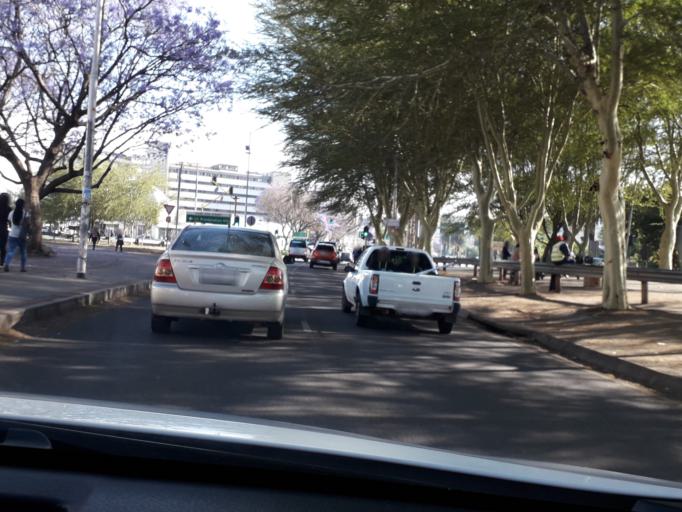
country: ZA
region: Gauteng
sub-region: City of Tshwane Metropolitan Municipality
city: Pretoria
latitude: -25.7508
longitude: 28.1982
